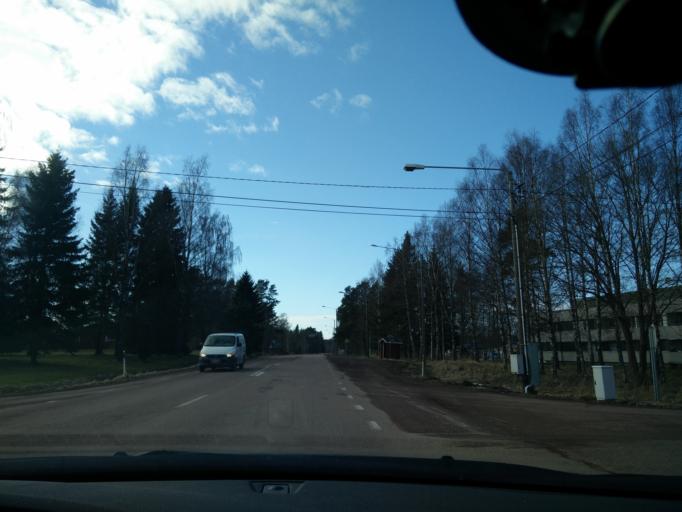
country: AX
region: Alands landsbygd
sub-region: Hammarland
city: Hammarland
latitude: 60.2164
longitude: 19.7406
